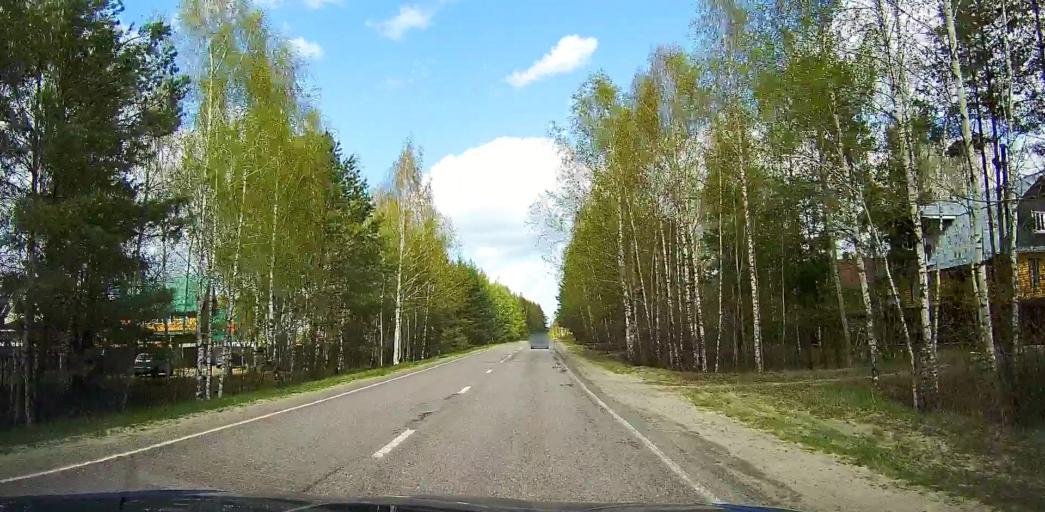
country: RU
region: Moskovskaya
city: Davydovo
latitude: 55.5900
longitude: 38.8318
